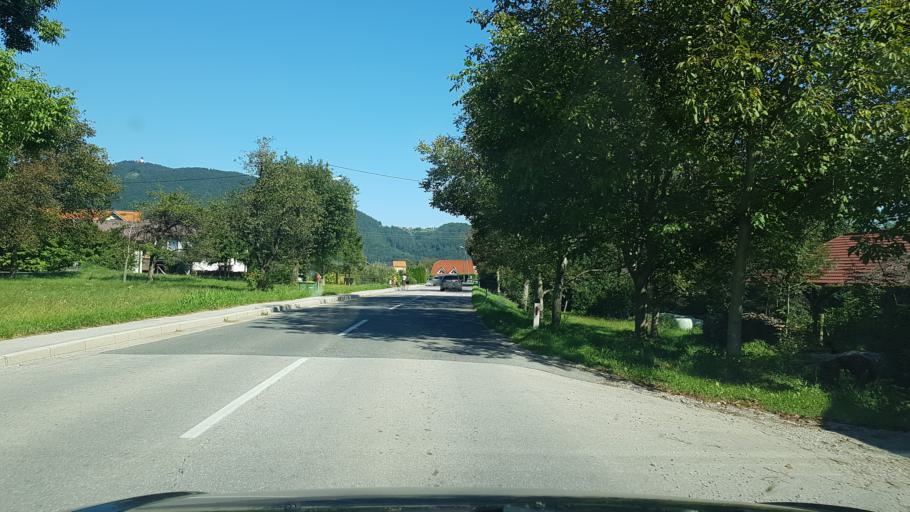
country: SI
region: Smartno ob Paki
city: Smartno ob Paki
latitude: 46.3168
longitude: 15.0222
